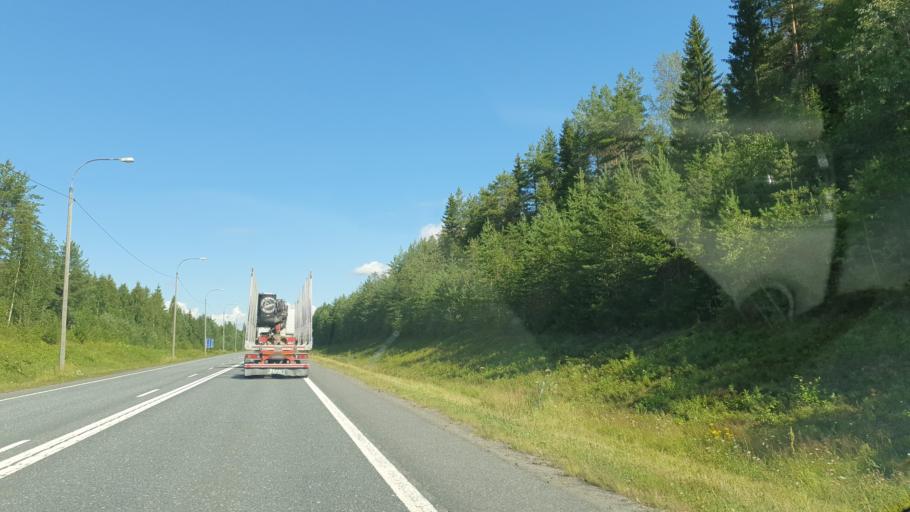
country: FI
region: Northern Savo
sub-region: Ylae-Savo
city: Iisalmi
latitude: 63.6123
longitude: 27.2193
